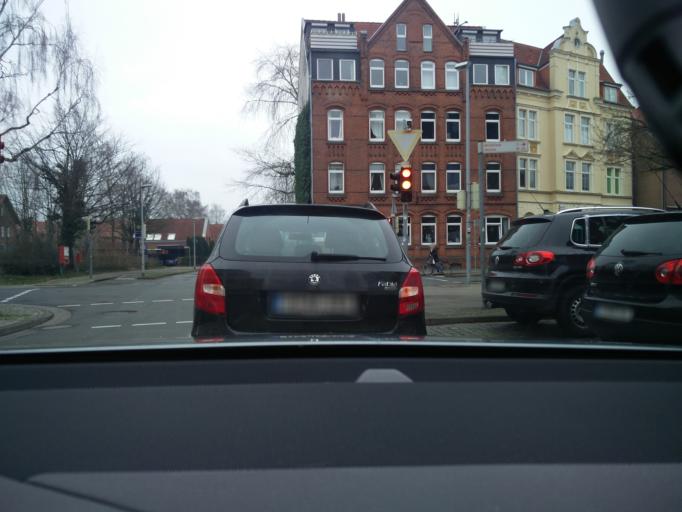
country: DE
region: Lower Saxony
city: Laatzen
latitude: 52.3333
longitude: 9.7649
